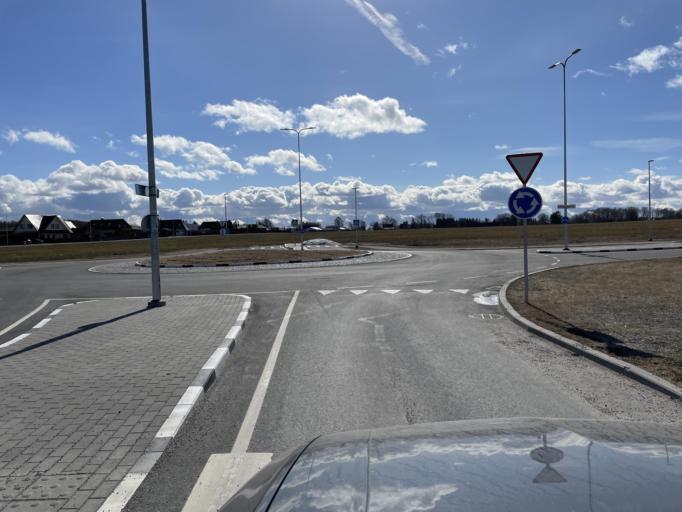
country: EE
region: Harju
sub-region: Rae vald
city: Jueri
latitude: 59.3783
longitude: 24.8298
